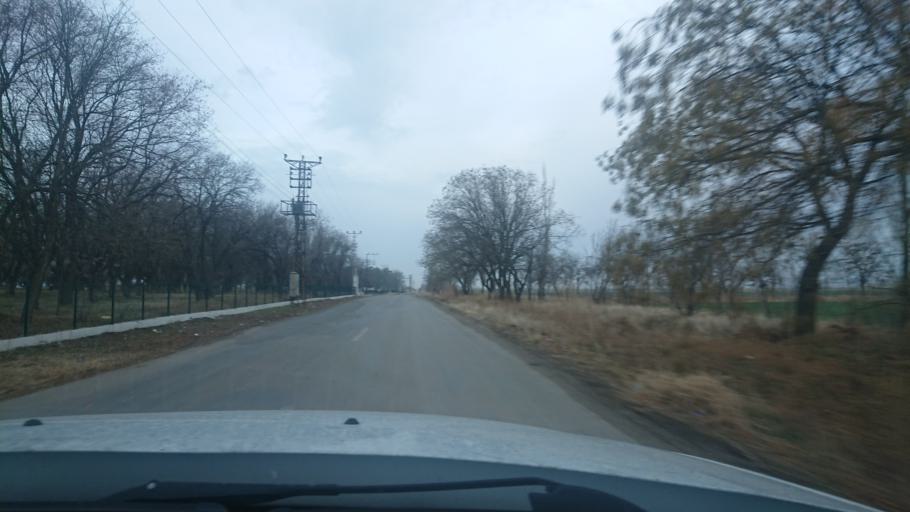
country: TR
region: Aksaray
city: Yesilova
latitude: 38.4608
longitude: 33.8420
